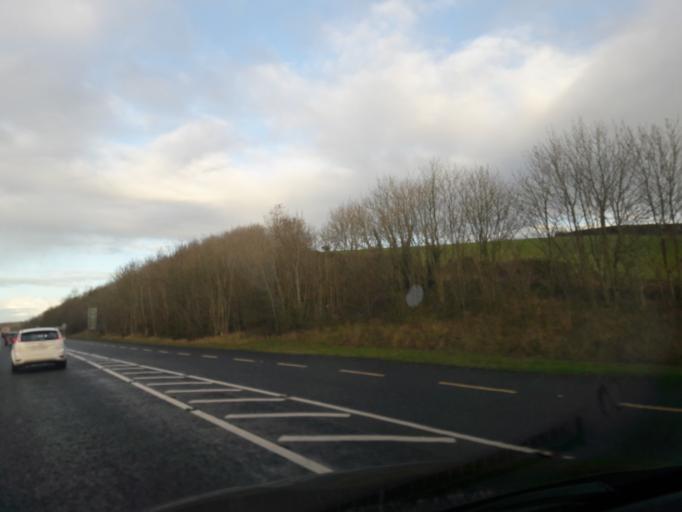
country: IE
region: Ulster
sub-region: County Monaghan
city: Carrickmacross
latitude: 53.9980
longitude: -6.7165
